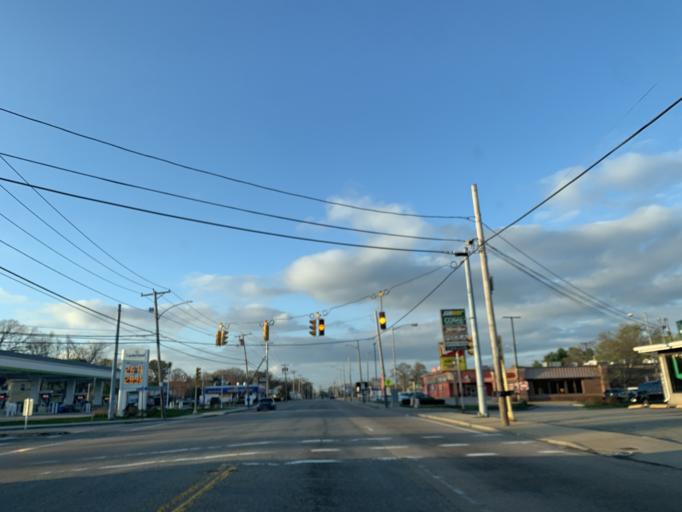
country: US
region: Rhode Island
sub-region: Providence County
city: Valley Falls
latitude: 41.9101
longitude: -71.3633
